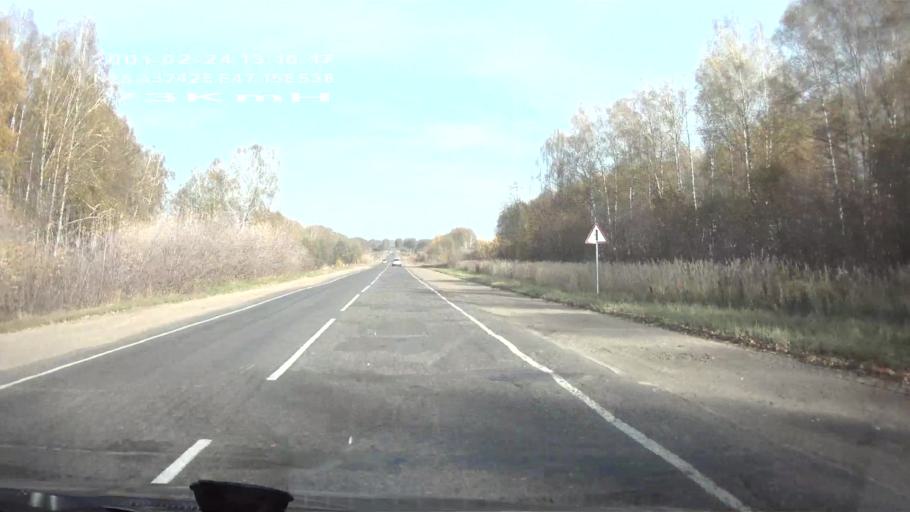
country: RU
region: Chuvashia
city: Ibresi
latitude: 55.3374
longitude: 47.1569
